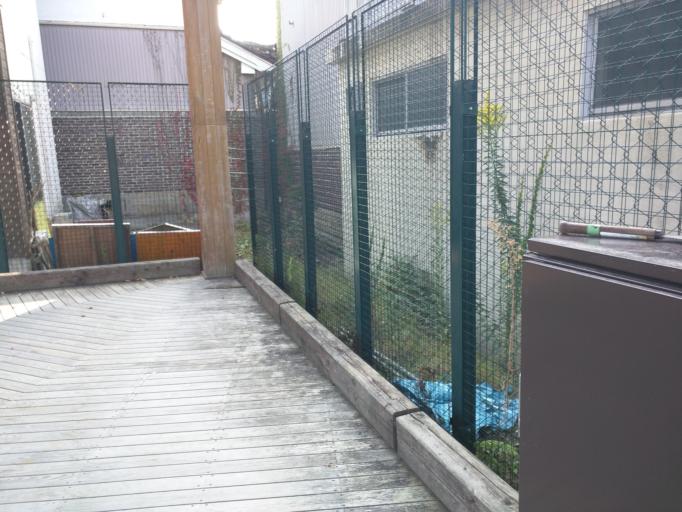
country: JP
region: Fukushima
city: Kitakata
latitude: 37.4992
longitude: 139.9248
